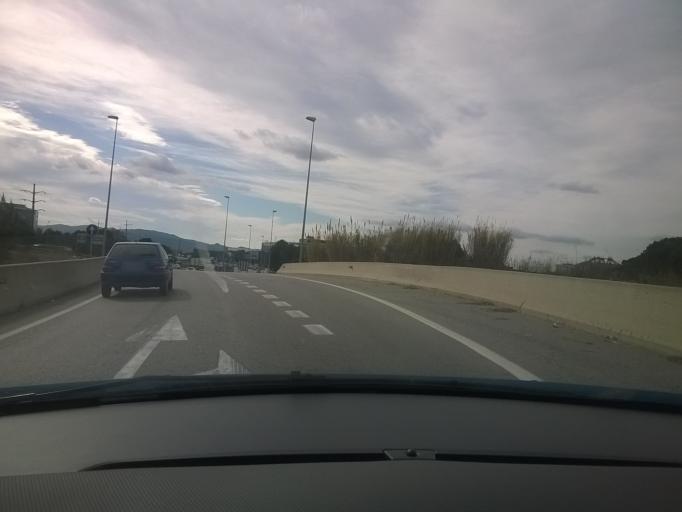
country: ES
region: Catalonia
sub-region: Provincia de Barcelona
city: Rubi
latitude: 41.4901
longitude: 2.0622
